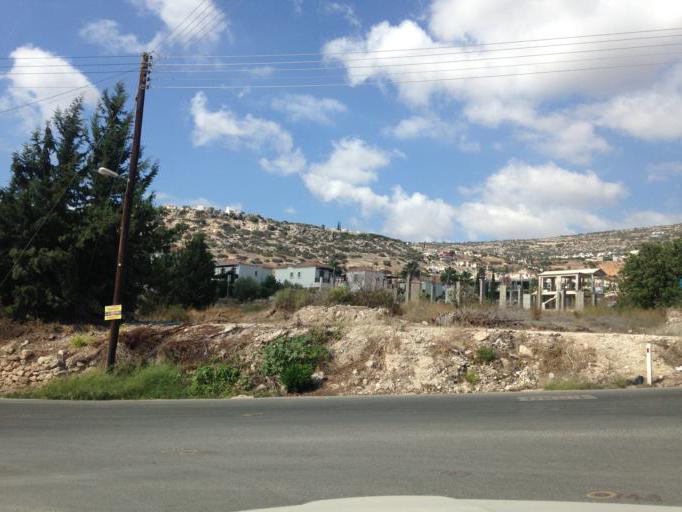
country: CY
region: Pafos
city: Pegeia
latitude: 34.8762
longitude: 32.3682
